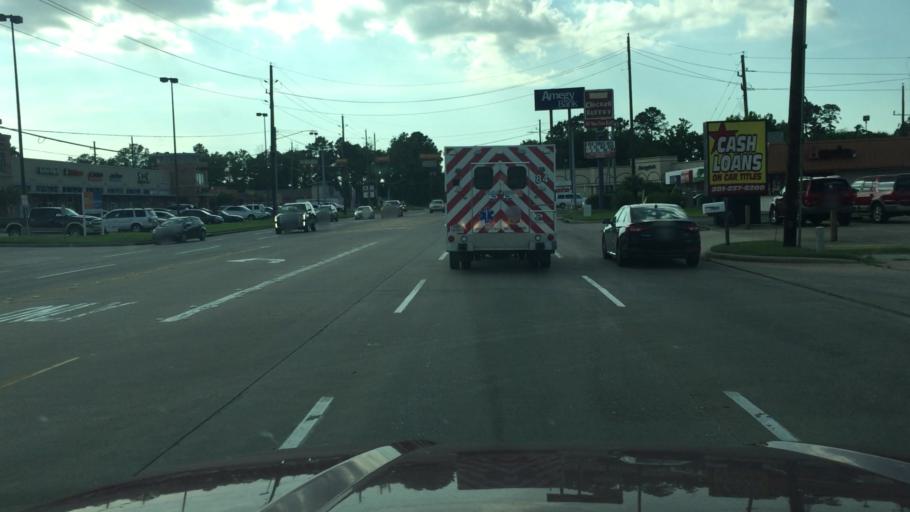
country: US
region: Texas
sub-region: Harris County
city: Tomball
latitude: 30.0225
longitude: -95.5256
